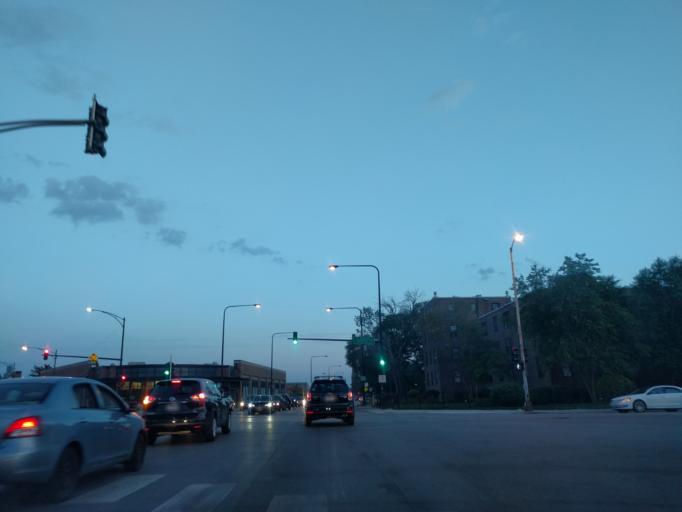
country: US
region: Illinois
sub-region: Cook County
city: Chicago
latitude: 41.9325
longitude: -87.6782
